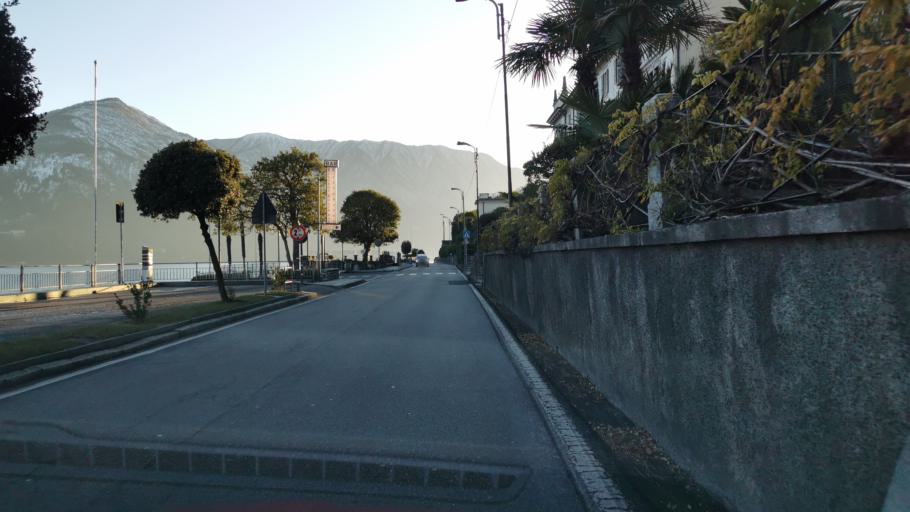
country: IT
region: Lombardy
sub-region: Provincia di Como
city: Cadenabbia
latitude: 45.9900
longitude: 9.2368
